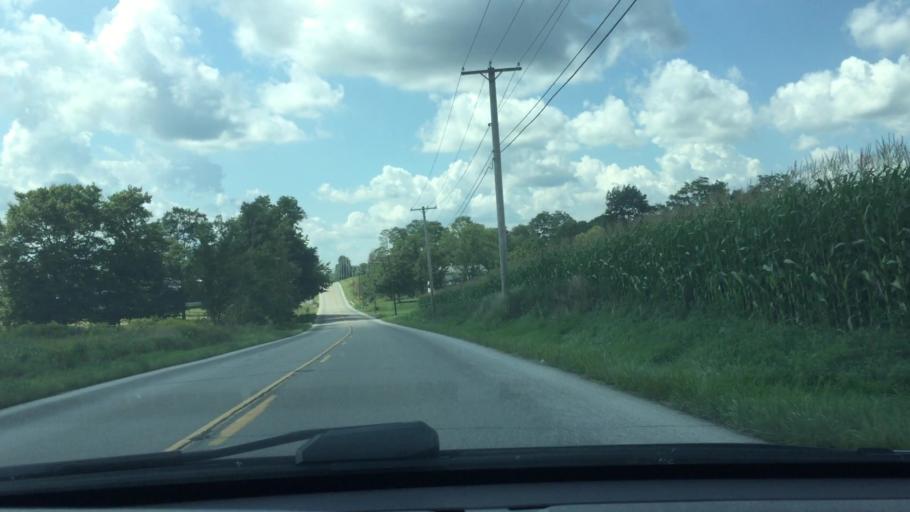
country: US
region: Pennsylvania
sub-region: Lawrence County
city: New Wilmington
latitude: 41.1203
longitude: -80.3869
